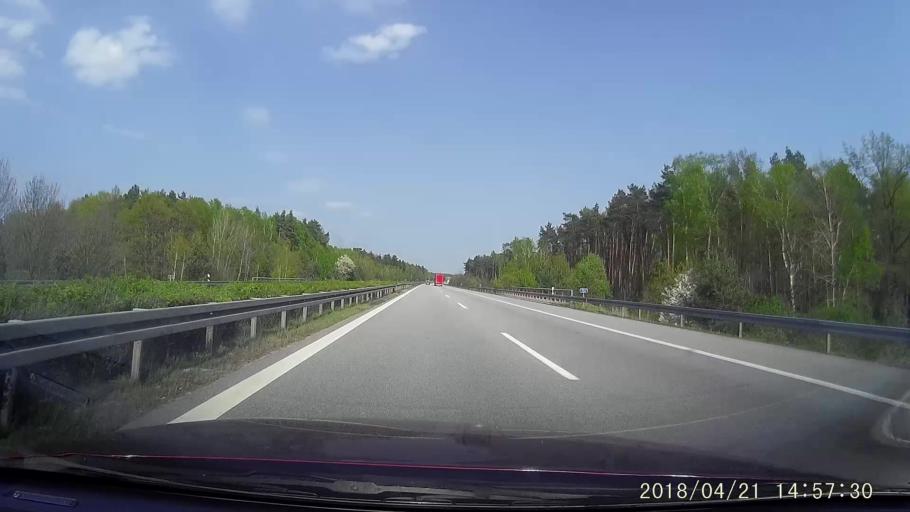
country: DE
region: Saxony
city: Weissenberg
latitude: 51.2114
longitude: 14.7053
